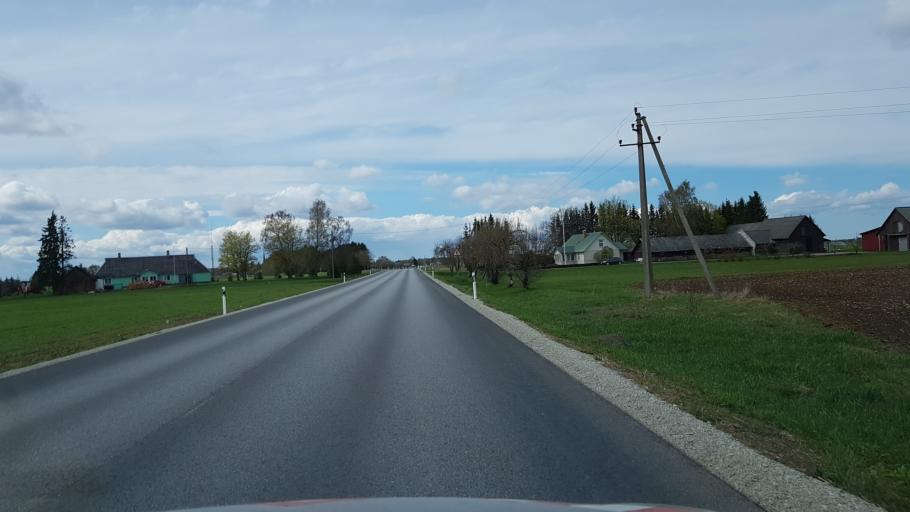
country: EE
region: Laeaene-Virumaa
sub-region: Vinni vald
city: Vinni
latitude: 59.2380
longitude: 26.4934
